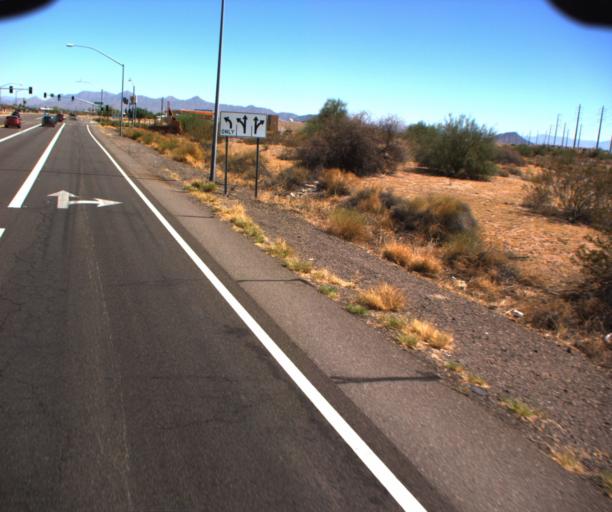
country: US
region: Arizona
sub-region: Maricopa County
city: Mesa
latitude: 33.4645
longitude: -111.8433
